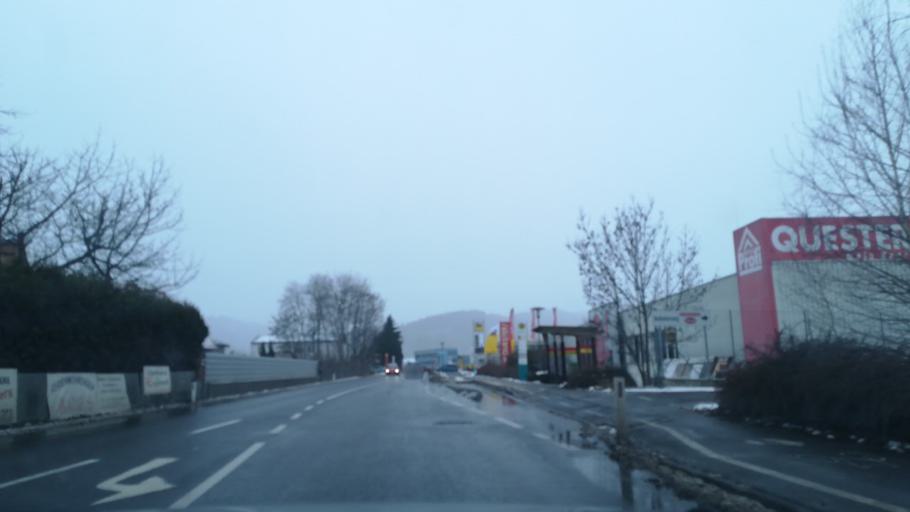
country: AT
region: Styria
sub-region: Politischer Bezirk Murtal
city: Judenburg
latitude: 47.1825
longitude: 14.6753
